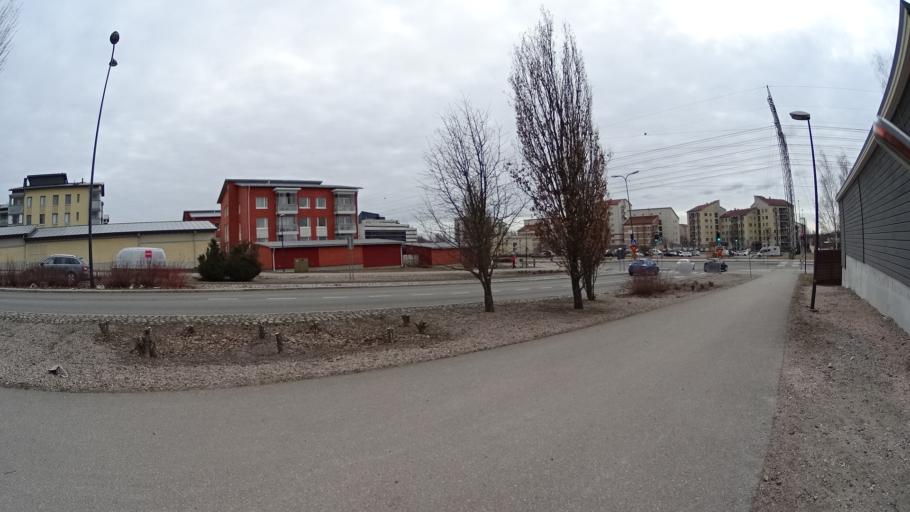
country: FI
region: Uusimaa
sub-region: Helsinki
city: Vantaa
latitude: 60.2903
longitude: 24.9439
